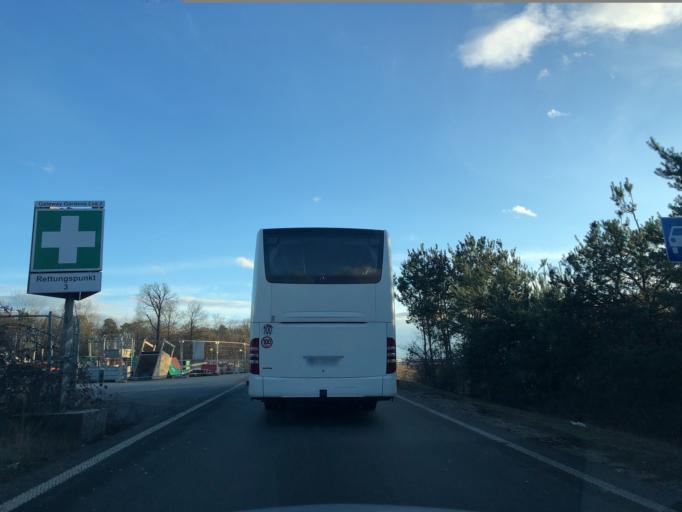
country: DE
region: Hesse
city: Niederrad
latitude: 50.0580
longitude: 8.6084
